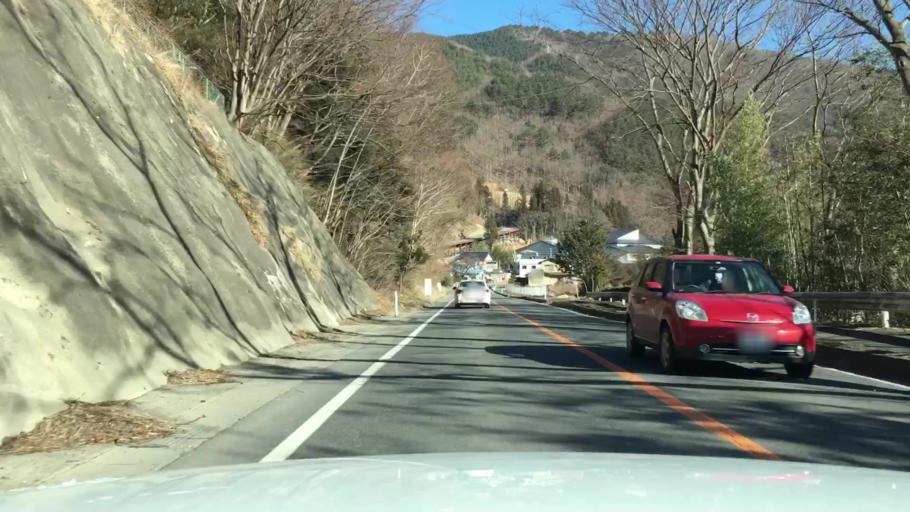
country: JP
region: Iwate
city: Miyako
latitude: 39.5961
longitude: 141.6768
